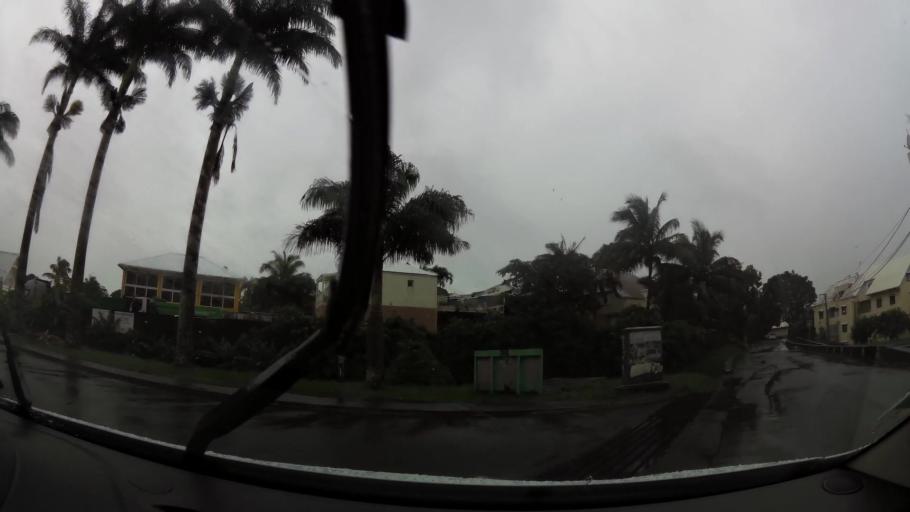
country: RE
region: Reunion
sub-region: Reunion
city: Saint-Andre
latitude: -20.9635
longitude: 55.6457
